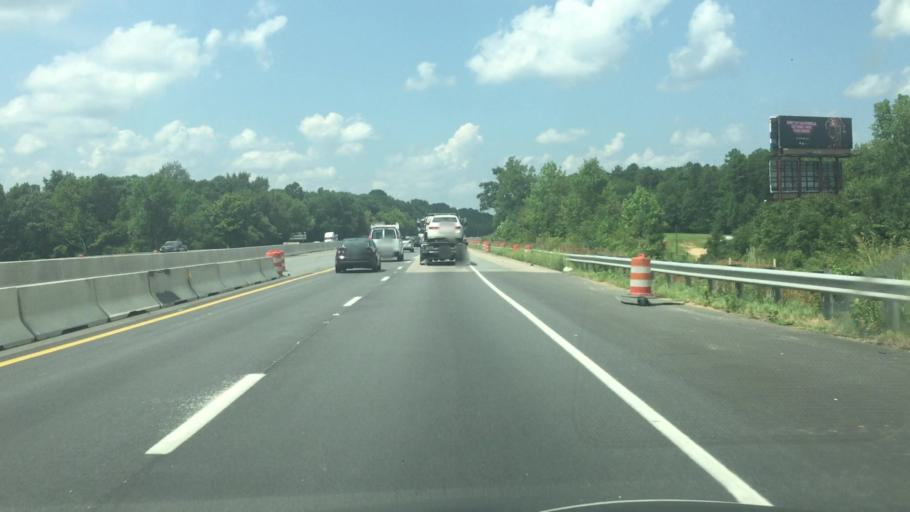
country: US
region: North Carolina
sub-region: Rowan County
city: Landis
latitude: 35.5105
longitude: -80.5653
